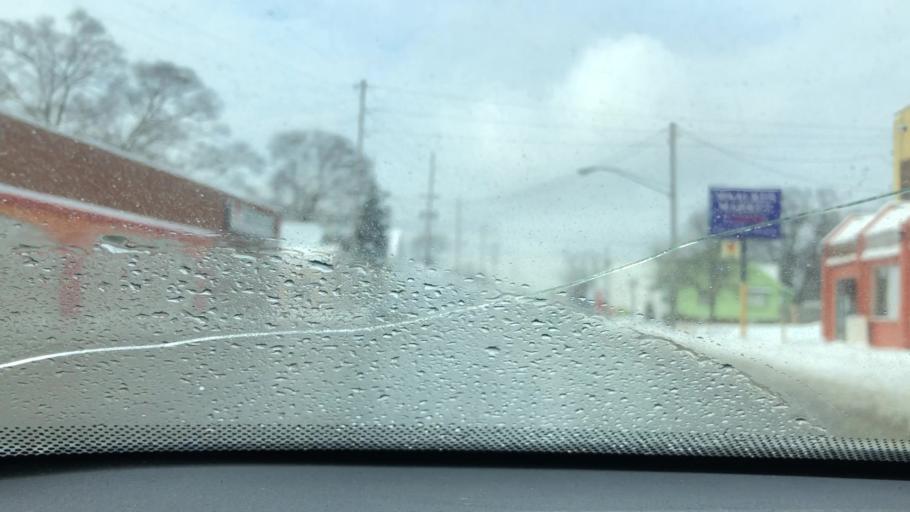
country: US
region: Michigan
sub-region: Kent County
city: Wyoming
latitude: 42.9354
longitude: -85.6971
